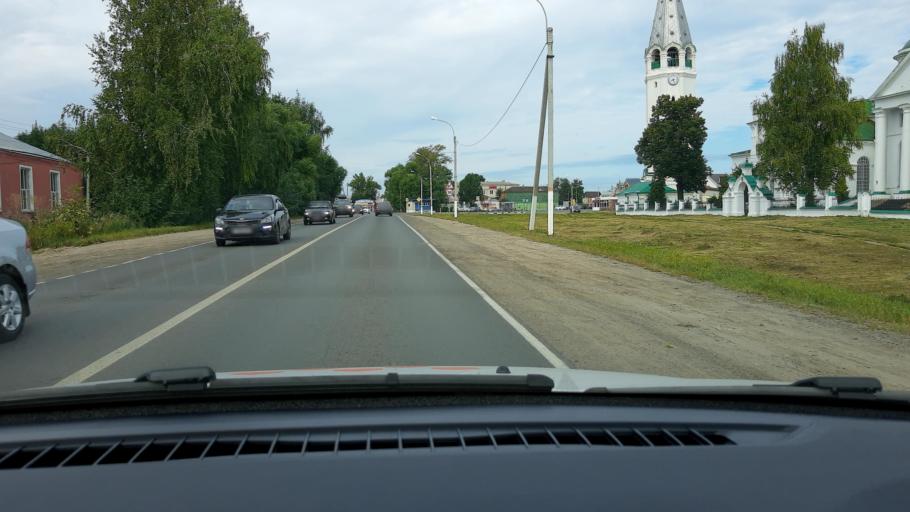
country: RU
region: Nizjnij Novgorod
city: Vyyezdnoye
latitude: 55.3835
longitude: 43.7987
